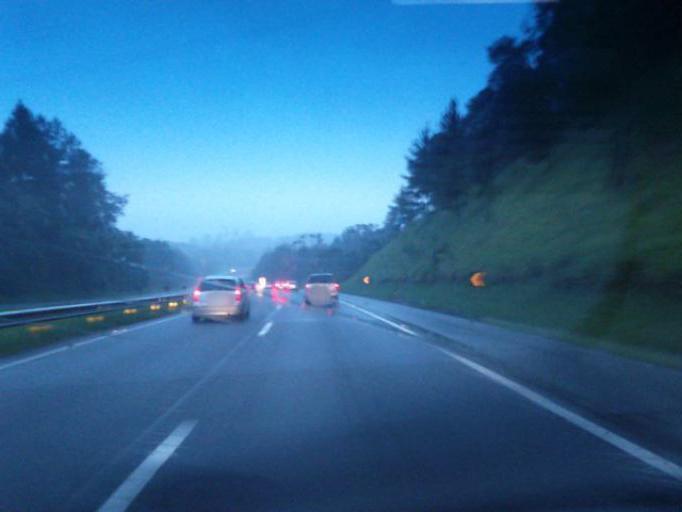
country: BR
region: Sao Paulo
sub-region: Juquitiba
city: Juquitiba
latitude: -23.9726
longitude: -47.1361
